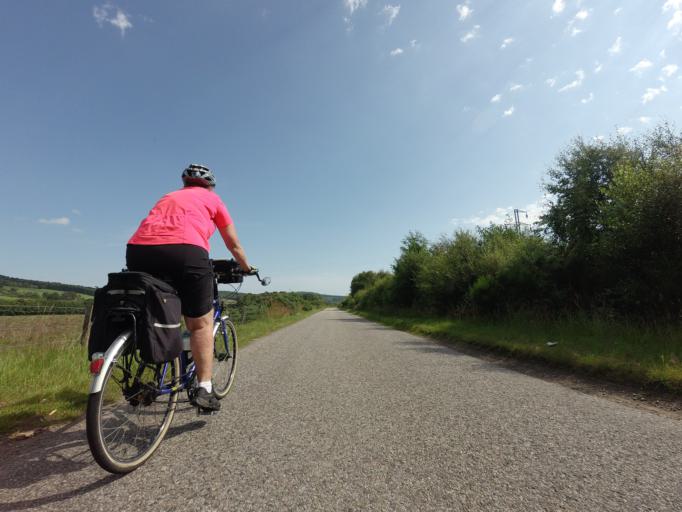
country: GB
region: Scotland
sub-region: Highland
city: Invergordon
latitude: 57.7414
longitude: -4.1799
